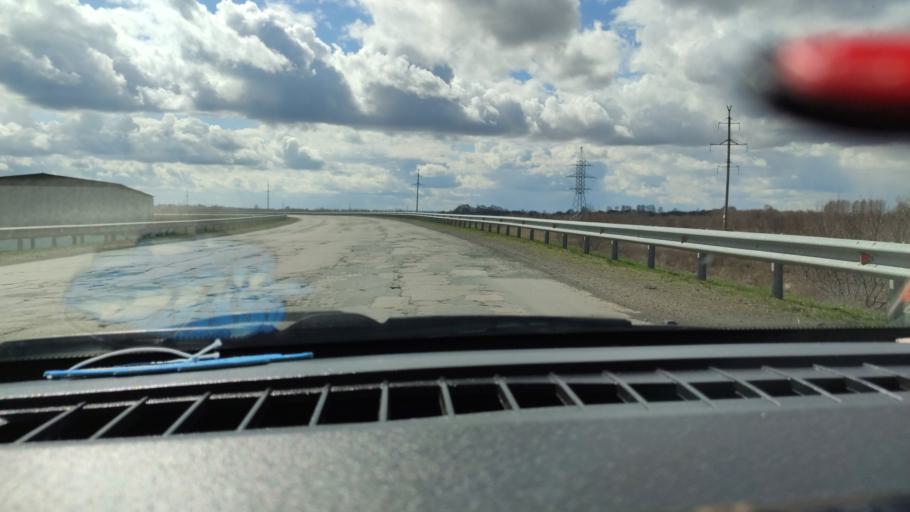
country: RU
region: Samara
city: Tol'yatti
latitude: 53.6689
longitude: 49.4160
